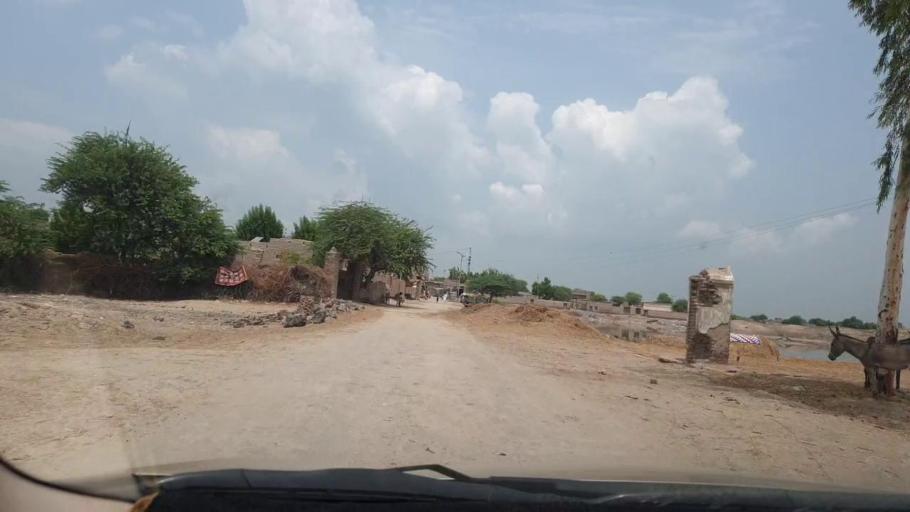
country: PK
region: Sindh
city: Larkana
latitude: 27.5591
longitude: 68.1235
